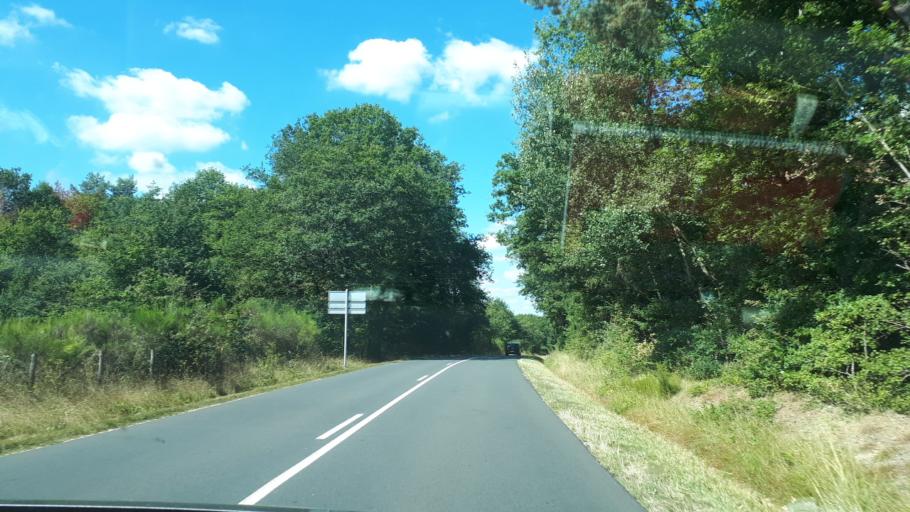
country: FR
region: Centre
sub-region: Departement du Loir-et-Cher
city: Saint-Viatre
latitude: 47.5745
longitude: 1.9632
